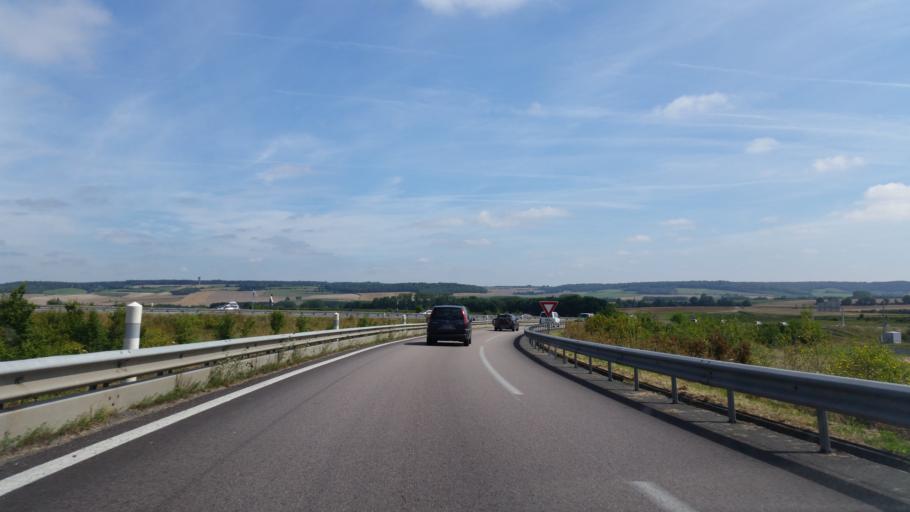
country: FR
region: Haute-Normandie
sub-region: Departement de la Seine-Maritime
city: Neufchatel-en-Bray
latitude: 49.7566
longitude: 1.4864
